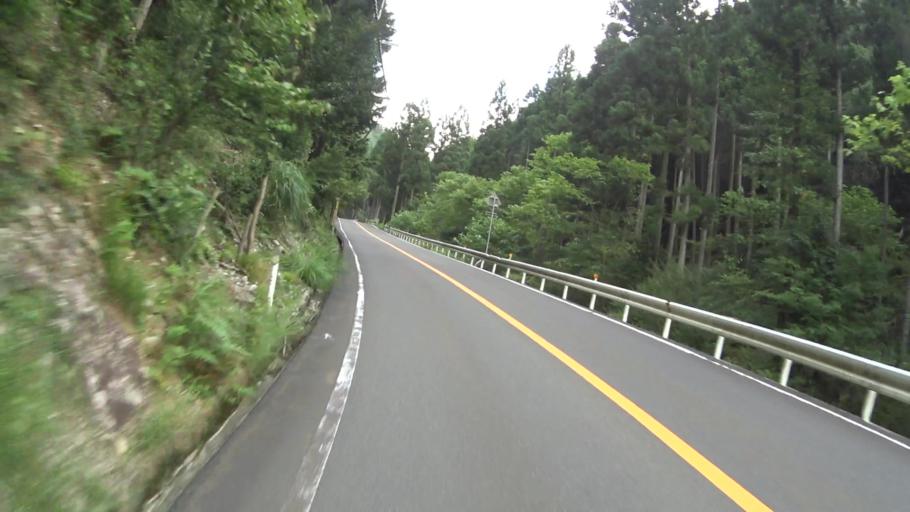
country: JP
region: Kyoto
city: Kameoka
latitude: 35.2577
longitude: 135.6147
